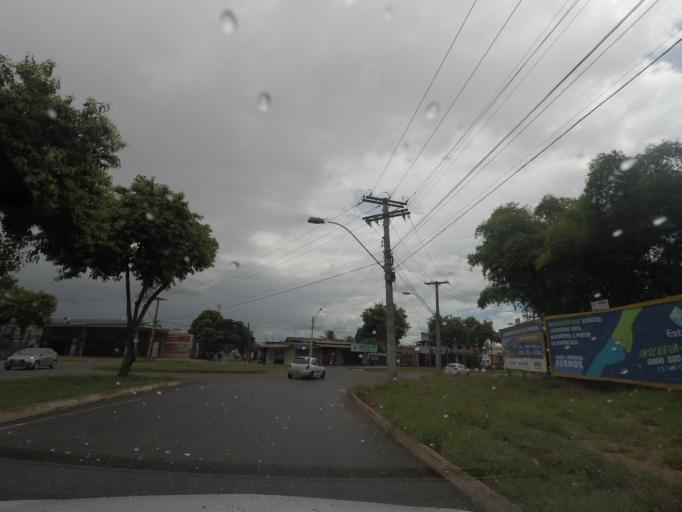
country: BR
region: Goias
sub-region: Goiania
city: Goiania
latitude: -16.7176
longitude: -49.3332
